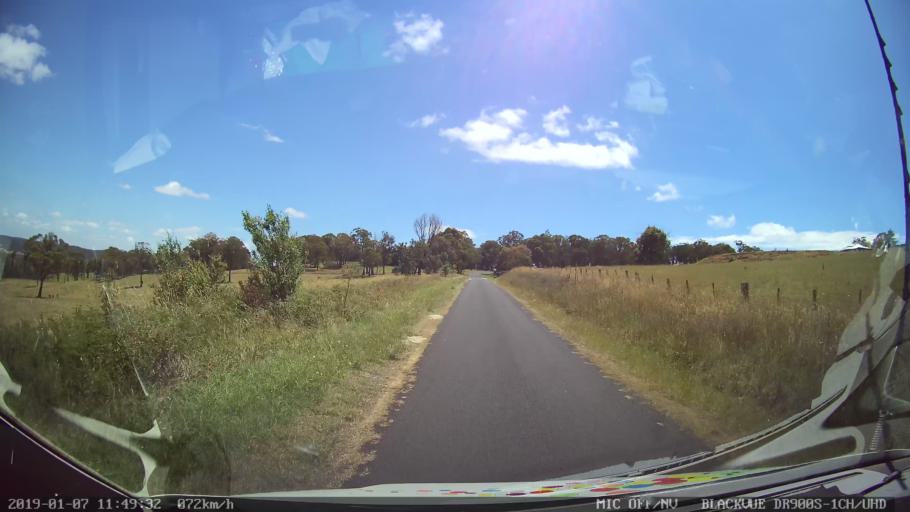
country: AU
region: New South Wales
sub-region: Guyra
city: Guyra
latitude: -30.3180
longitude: 151.6290
